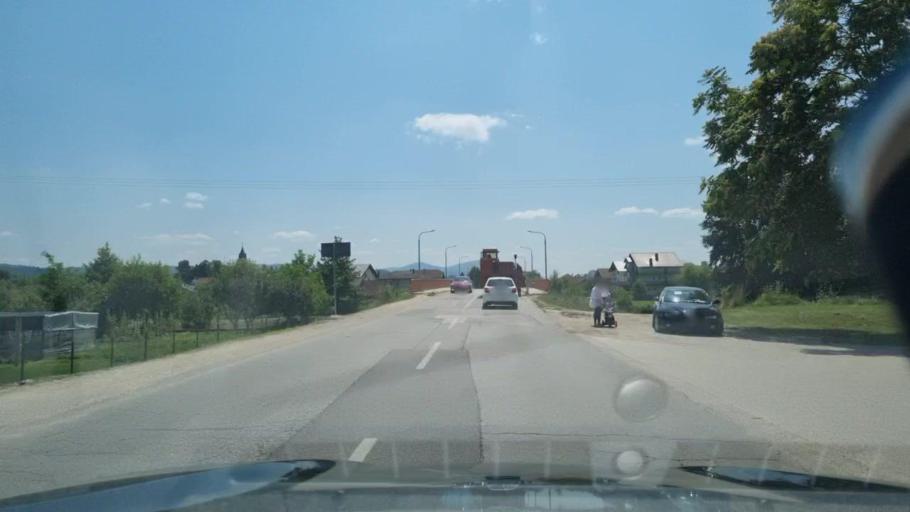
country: BA
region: Federation of Bosnia and Herzegovina
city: Sanski Most
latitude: 44.7708
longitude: 16.6684
